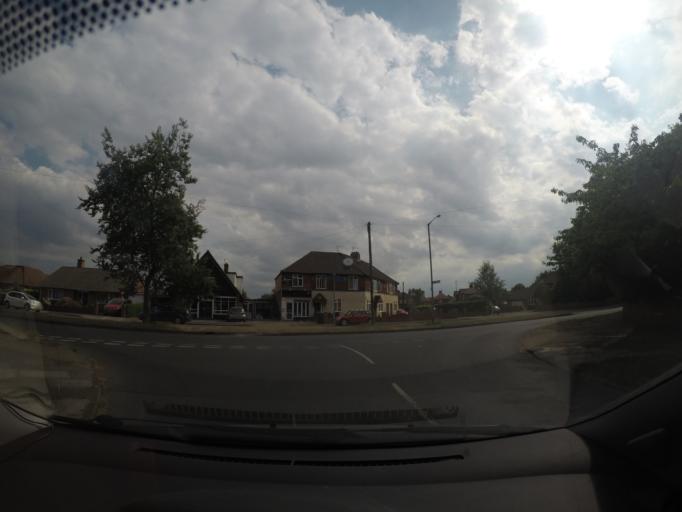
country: GB
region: England
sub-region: City of York
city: York
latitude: 53.9517
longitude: -1.1186
